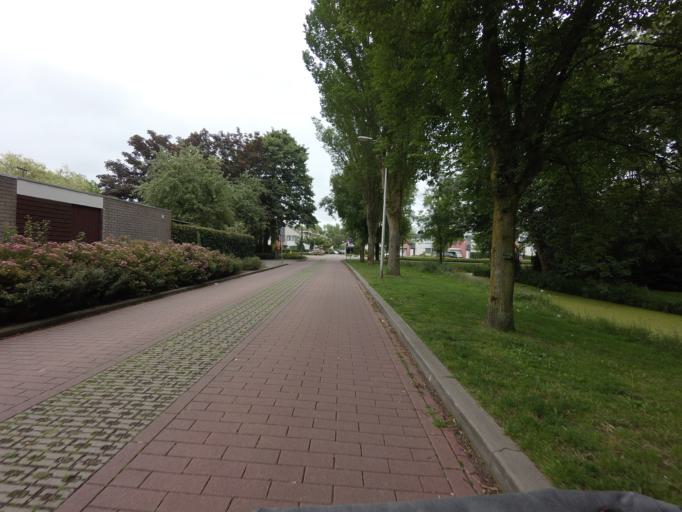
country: NL
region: South Holland
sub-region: Gemeente Wassenaar
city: Wassenaar
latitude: 52.1459
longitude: 4.4181
